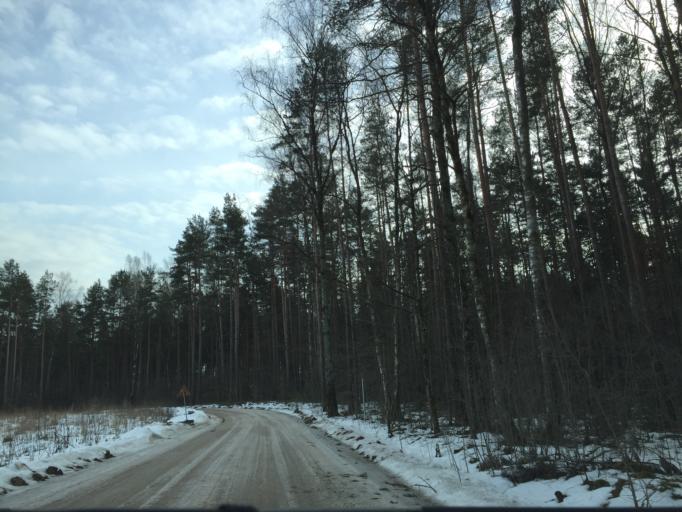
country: LV
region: Stopini
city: Ulbroka
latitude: 56.9250
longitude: 24.2838
